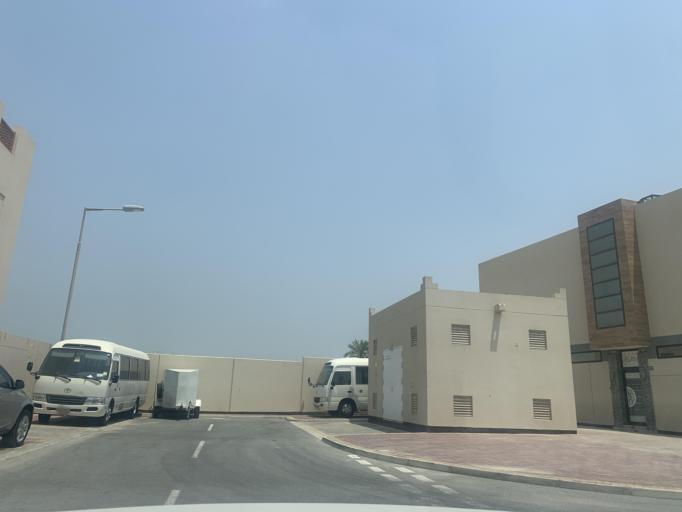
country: BH
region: Central Governorate
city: Madinat Hamad
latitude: 26.1452
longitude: 50.4640
